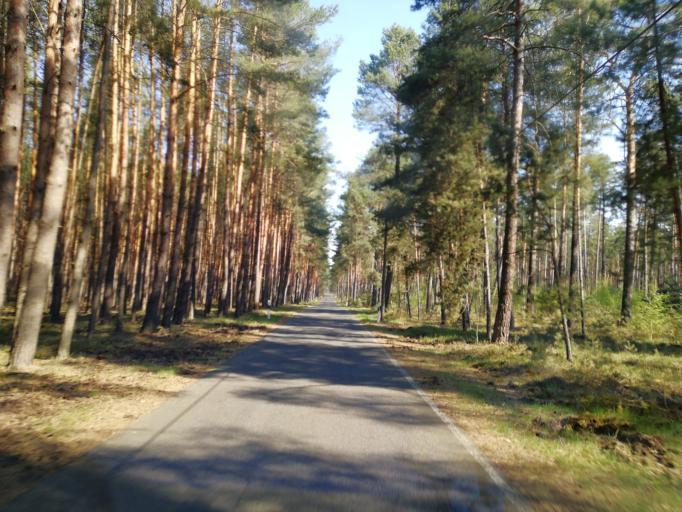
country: DE
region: Brandenburg
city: Bronkow
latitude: 51.6742
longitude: 13.8640
